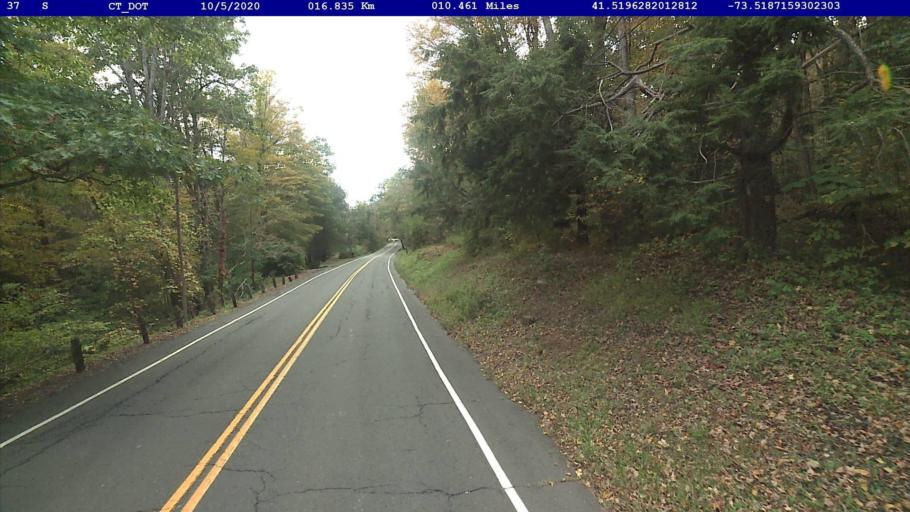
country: US
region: New York
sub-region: Putnam County
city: Putnam Lake
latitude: 41.5196
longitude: -73.5187
